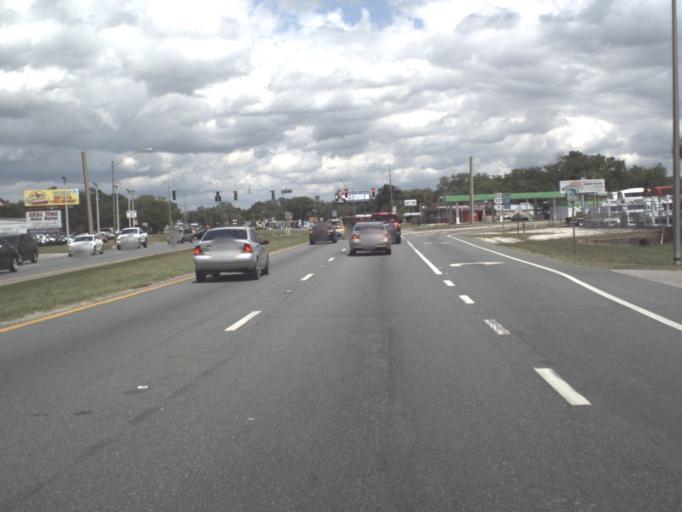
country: US
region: Florida
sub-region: Marion County
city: Ocala
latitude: 29.2051
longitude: -82.1418
